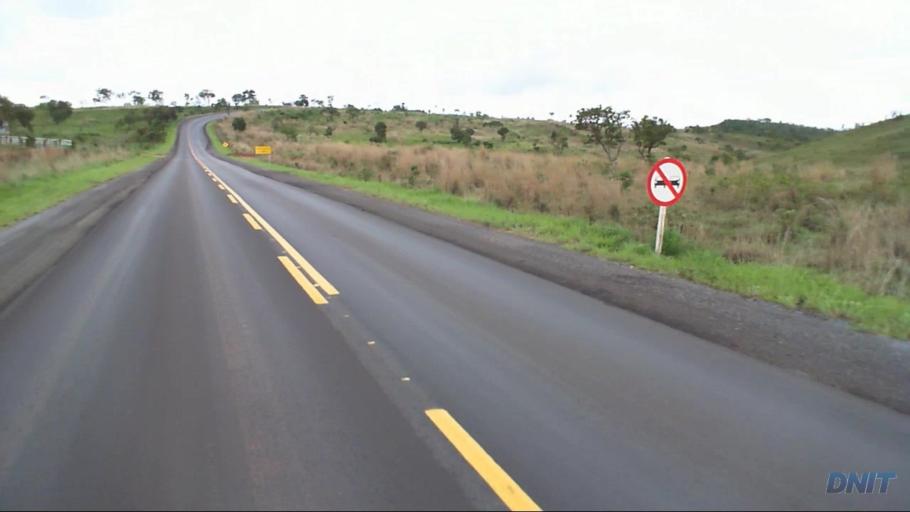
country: BR
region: Goias
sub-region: Padre Bernardo
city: Padre Bernardo
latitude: -15.2095
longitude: -48.4718
